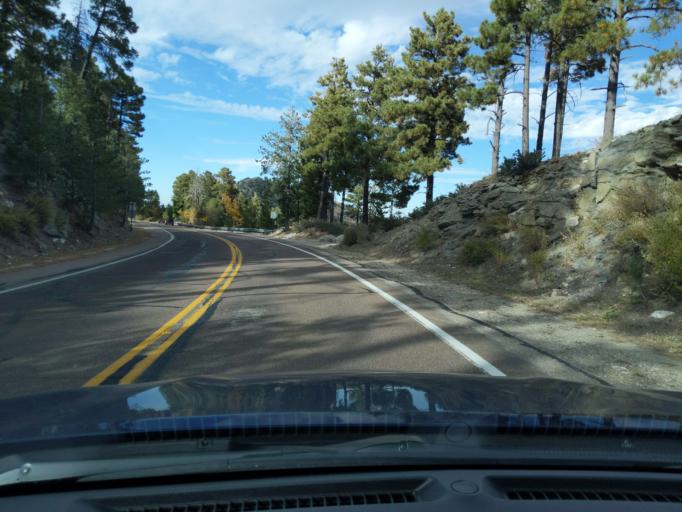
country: US
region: Arizona
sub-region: Pinal County
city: Oracle
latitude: 32.4453
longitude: -110.7530
